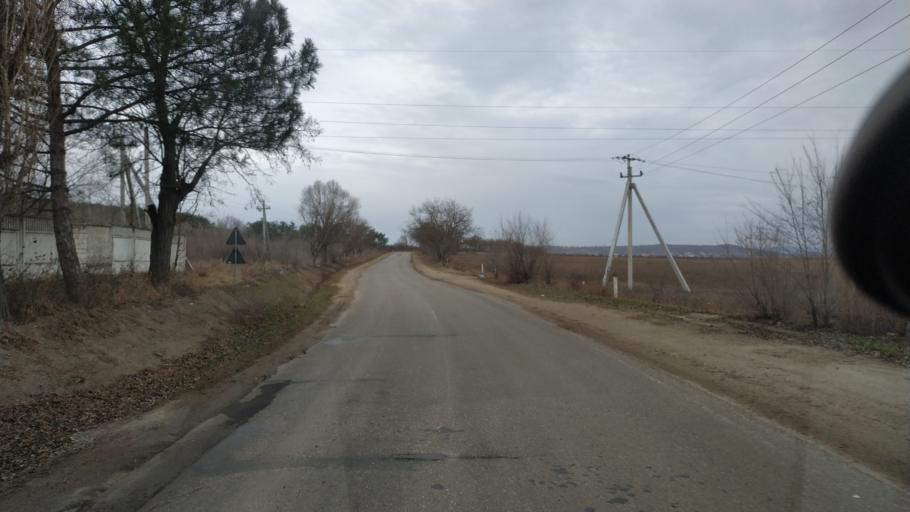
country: MD
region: Criuleni
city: Criuleni
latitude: 47.2406
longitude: 29.1494
